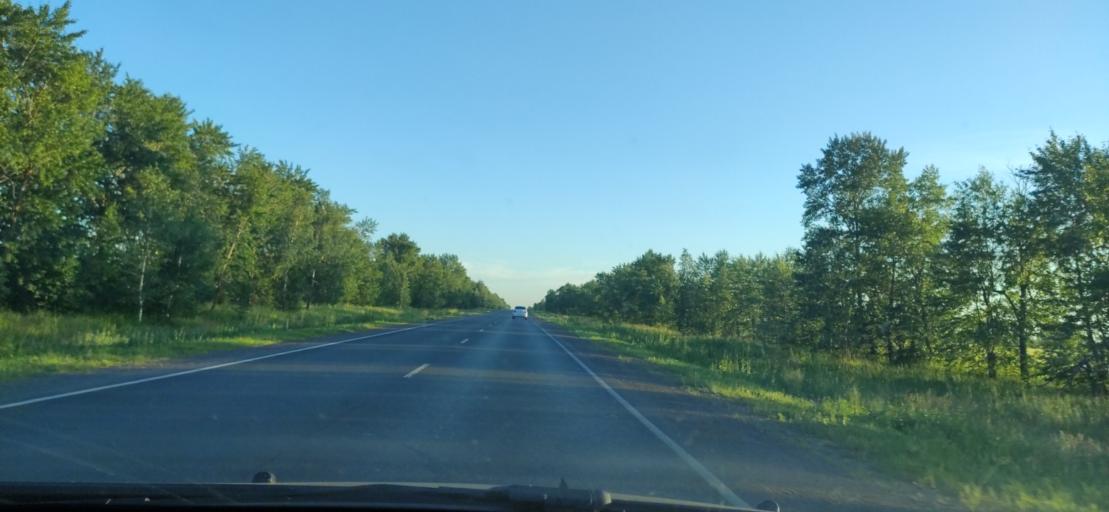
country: RU
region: Ulyanovsk
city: Cherdakly
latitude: 54.4109
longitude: 48.8785
